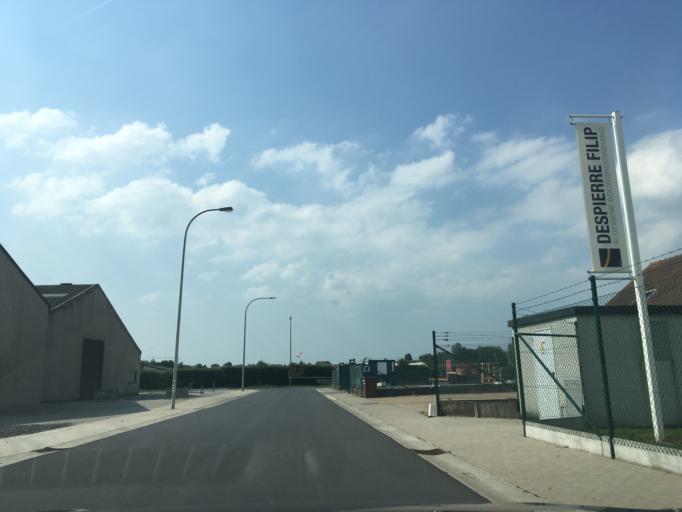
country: BE
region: Flanders
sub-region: Provincie West-Vlaanderen
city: Houthulst
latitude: 50.9688
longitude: 2.9409
